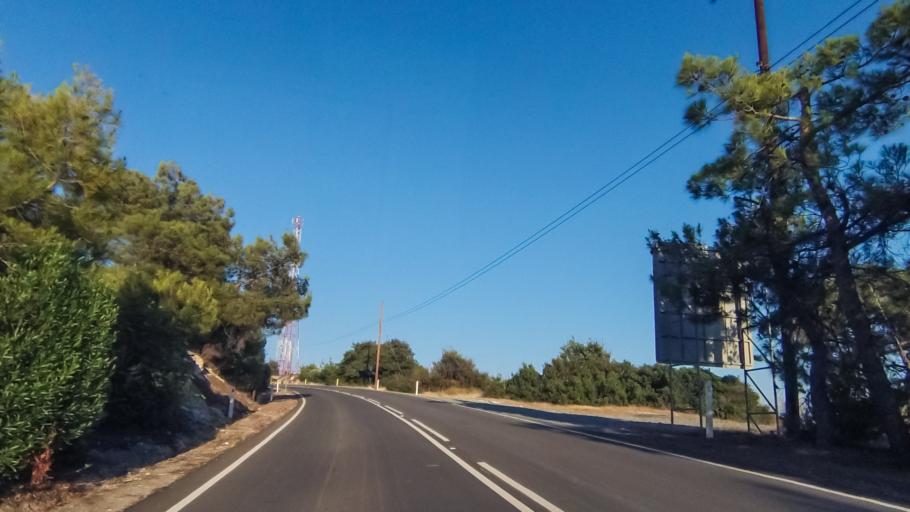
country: CY
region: Limassol
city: Sotira
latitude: 34.6754
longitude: 32.8025
